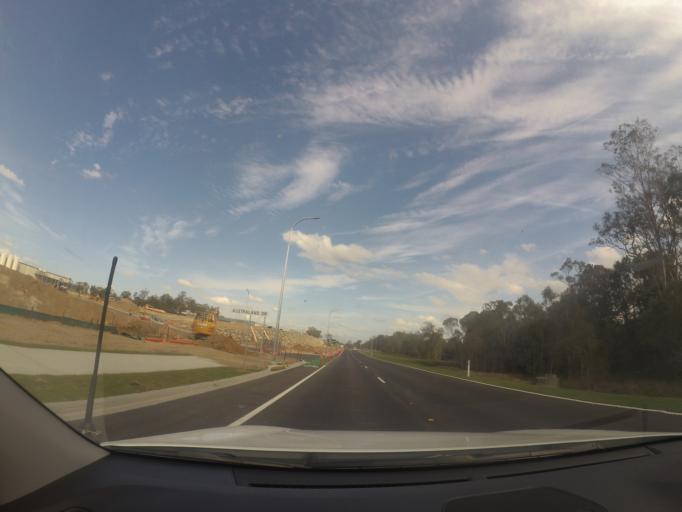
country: AU
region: Queensland
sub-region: Logan
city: Woodridge
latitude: -27.6500
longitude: 153.0871
